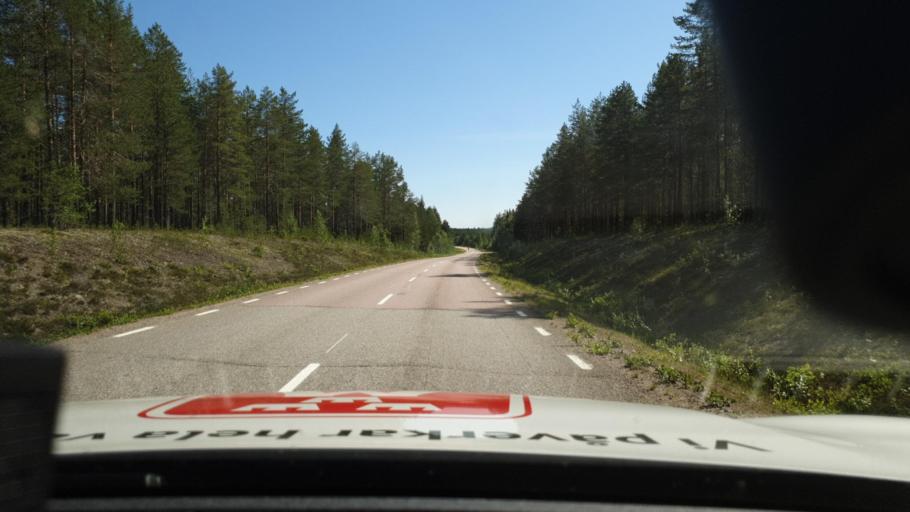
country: SE
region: Norrbotten
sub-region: Lulea Kommun
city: Ranea
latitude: 65.9713
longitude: 22.3789
